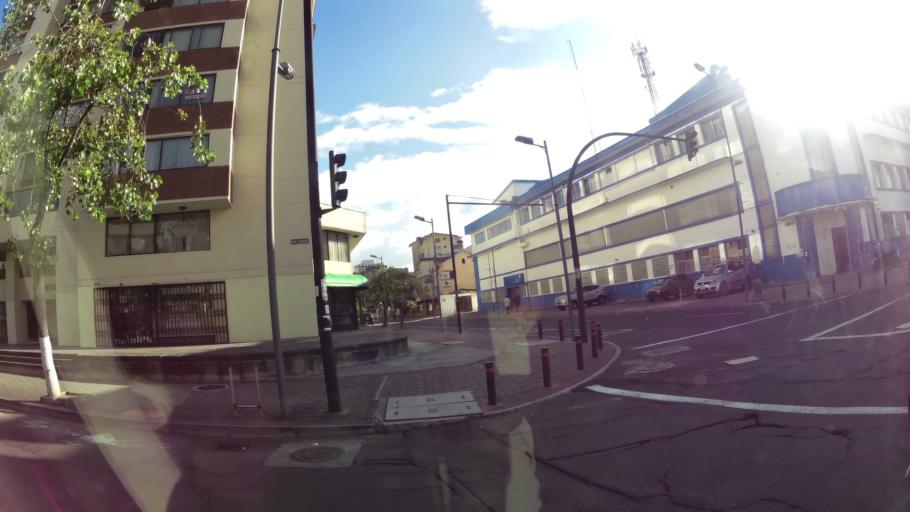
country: EC
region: Pichincha
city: Quito
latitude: -0.2045
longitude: -78.4928
